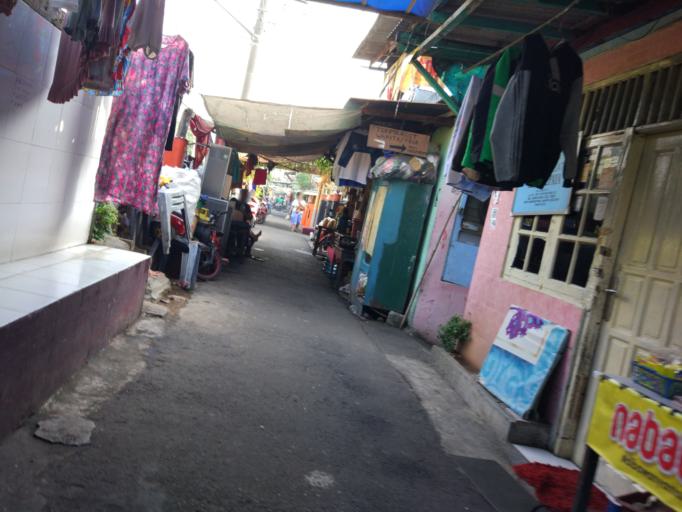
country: ID
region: Jakarta Raya
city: Jakarta
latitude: -6.2388
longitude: 106.8586
